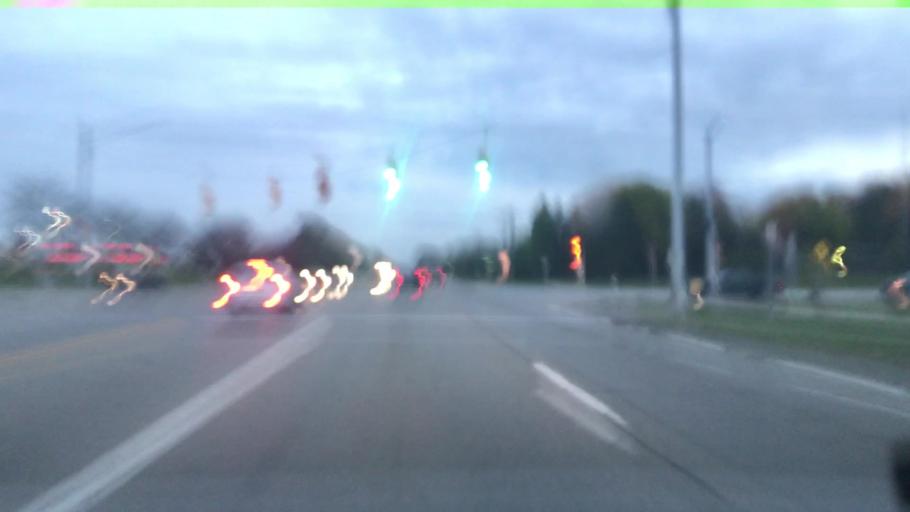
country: US
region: Michigan
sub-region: Oakland County
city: Bloomfield Hills
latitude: 42.6063
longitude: -83.2480
